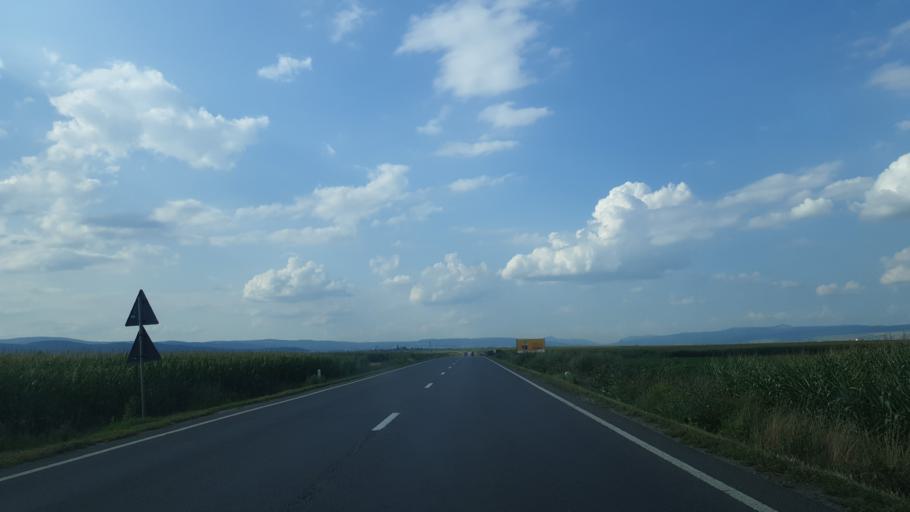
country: RO
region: Covasna
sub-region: Comuna Chichis
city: Chichis
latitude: 45.7855
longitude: 25.8073
